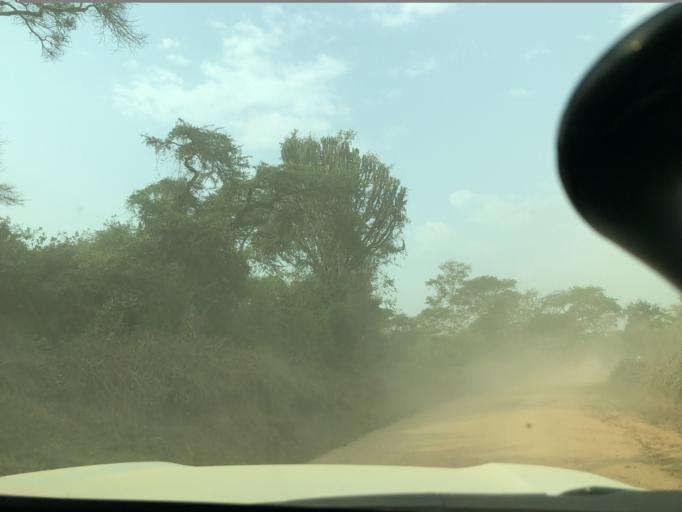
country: UG
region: Western Region
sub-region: Kasese District
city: Margherita
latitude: 0.1933
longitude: 29.6572
